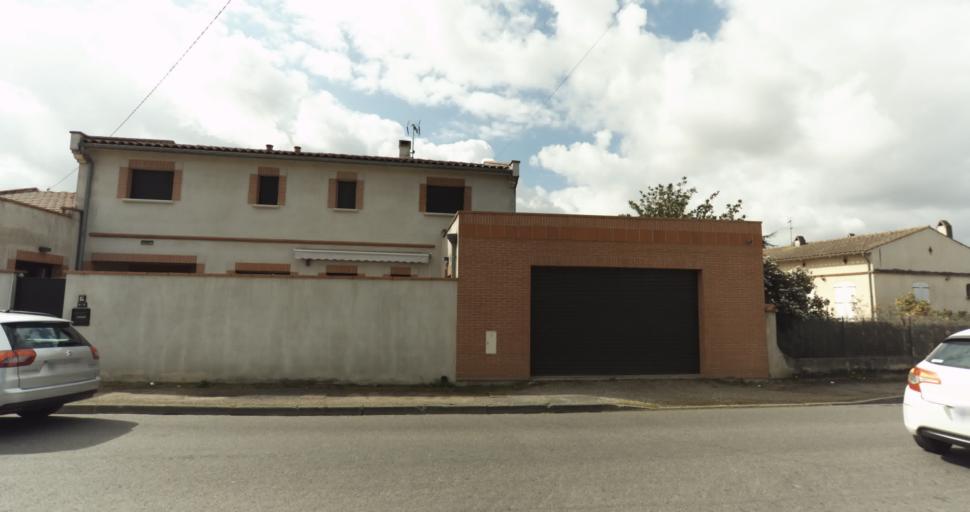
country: FR
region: Midi-Pyrenees
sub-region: Departement de la Haute-Garonne
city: Auterive
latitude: 43.3551
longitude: 1.4696
